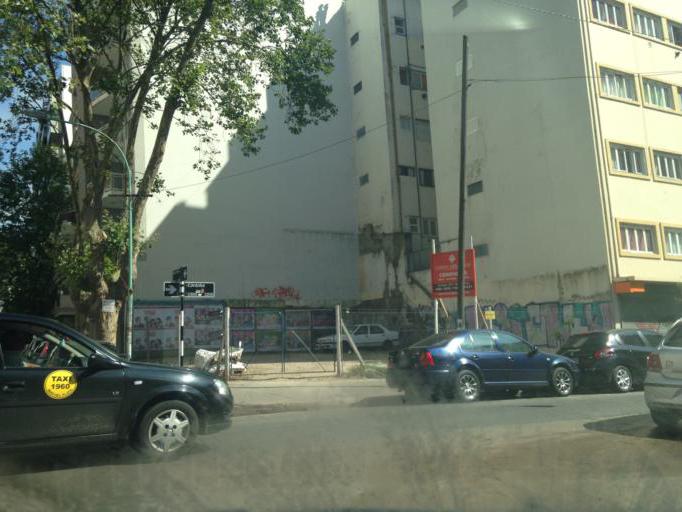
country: AR
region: Buenos Aires
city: Mar del Plata
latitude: -38.0044
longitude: -57.5507
